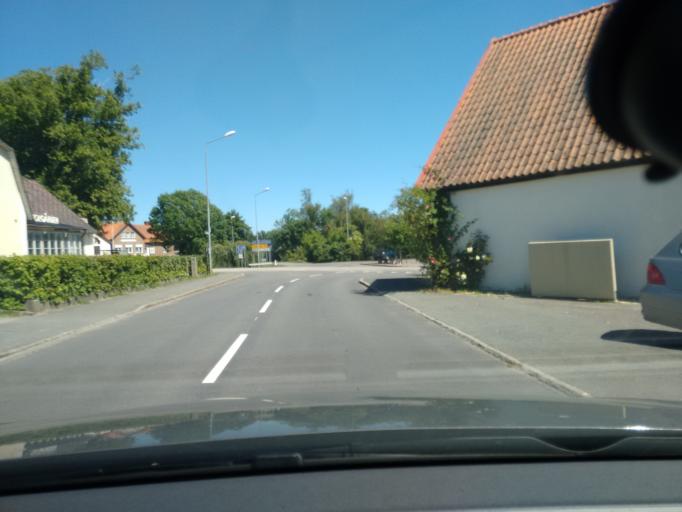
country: SE
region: Skane
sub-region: Kristianstads Kommun
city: Degeberga
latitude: 55.7722
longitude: 14.1506
